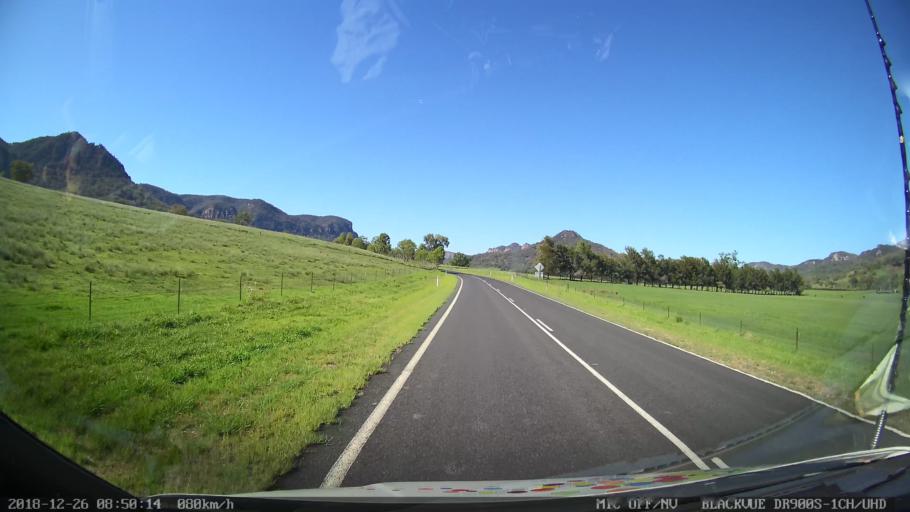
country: AU
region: New South Wales
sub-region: Mid-Western Regional
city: Kandos
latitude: -32.5732
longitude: 150.0962
